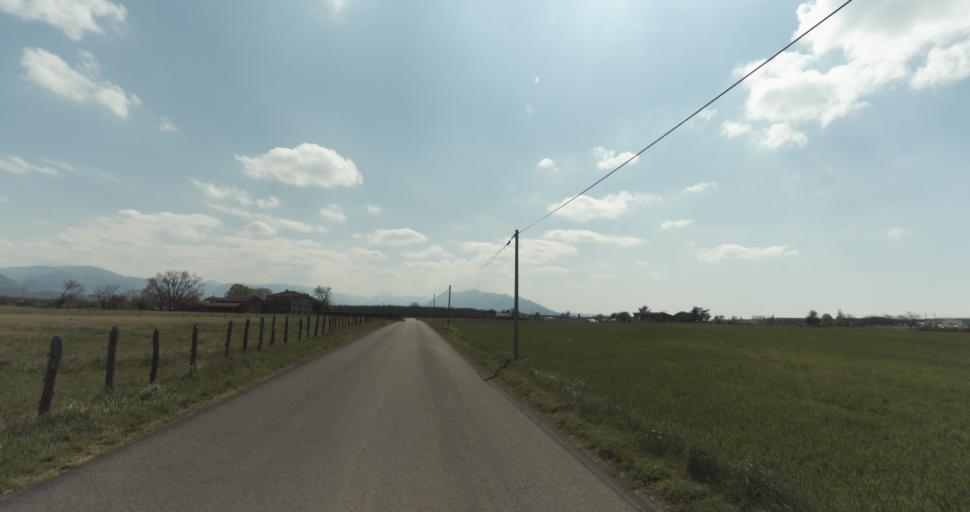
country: FR
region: Rhone-Alpes
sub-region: Departement de l'Isere
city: Saint-Marcellin
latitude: 45.1432
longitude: 5.3088
